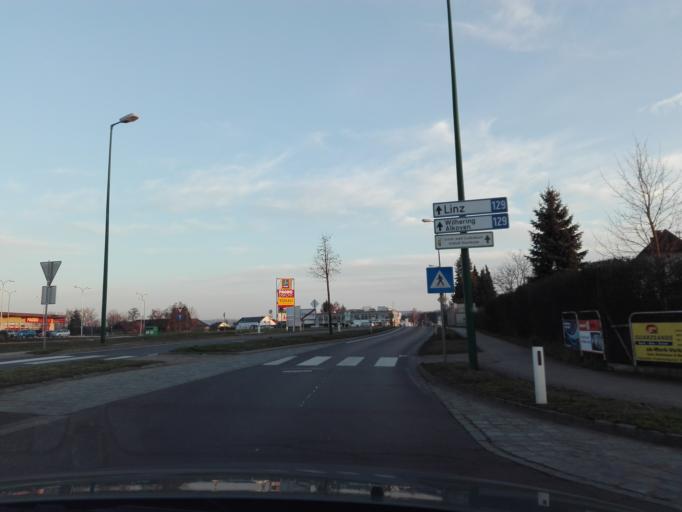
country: AT
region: Upper Austria
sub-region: Politischer Bezirk Urfahr-Umgebung
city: Feldkirchen an der Donau
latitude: 48.3019
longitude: 14.0302
